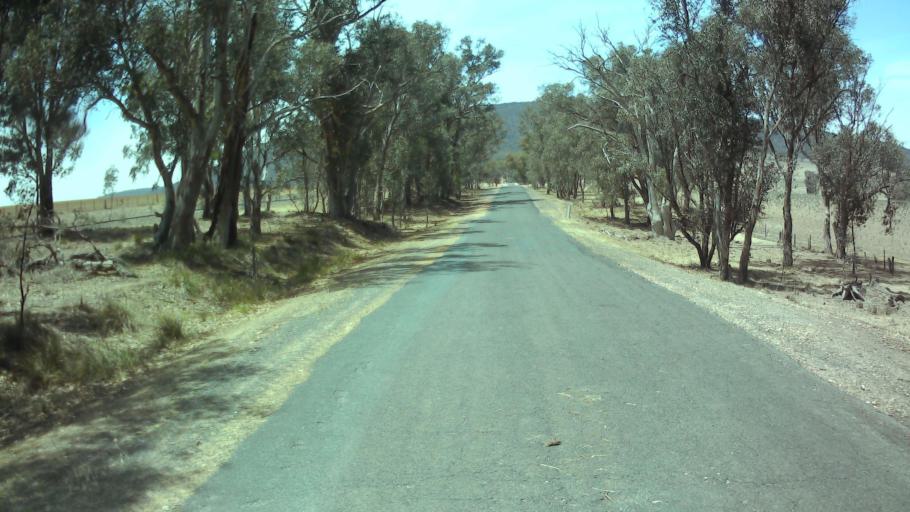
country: AU
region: New South Wales
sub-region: Weddin
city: Grenfell
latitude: -34.0298
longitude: 148.4324
